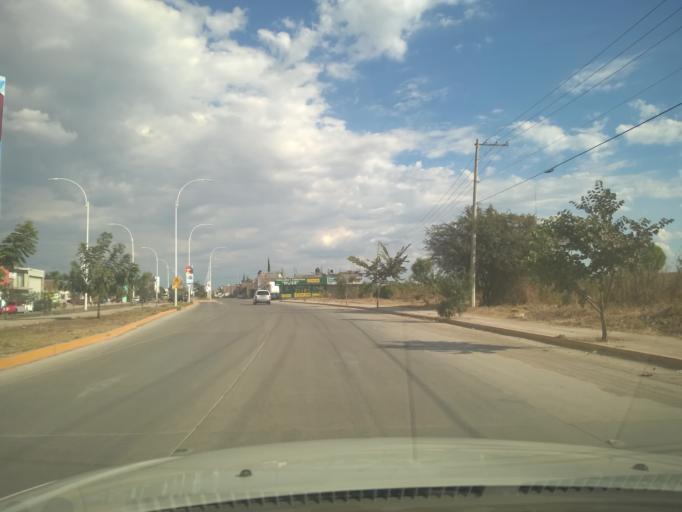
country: MX
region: Guanajuato
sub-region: Leon
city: San Jose de Duran (Los Troncoso)
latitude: 21.0650
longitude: -101.6326
